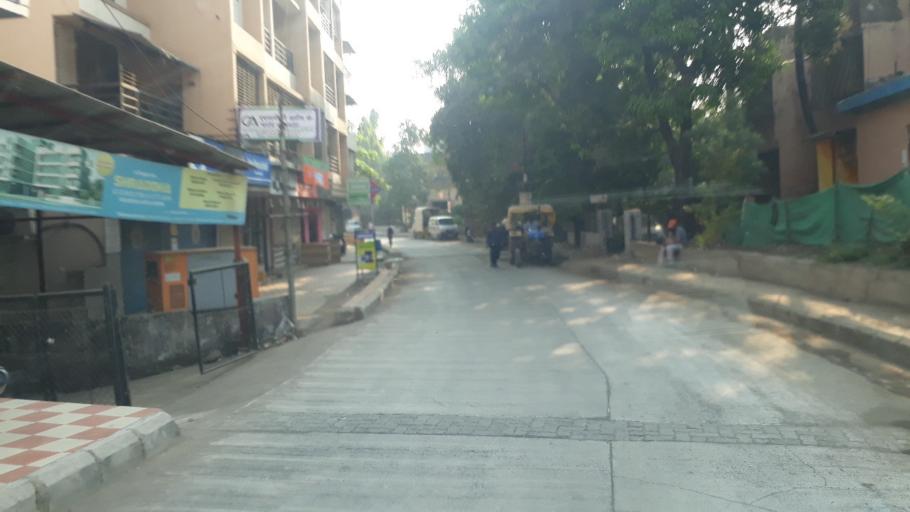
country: IN
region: Maharashtra
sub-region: Raigarh
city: Neral
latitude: 19.0226
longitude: 73.3143
